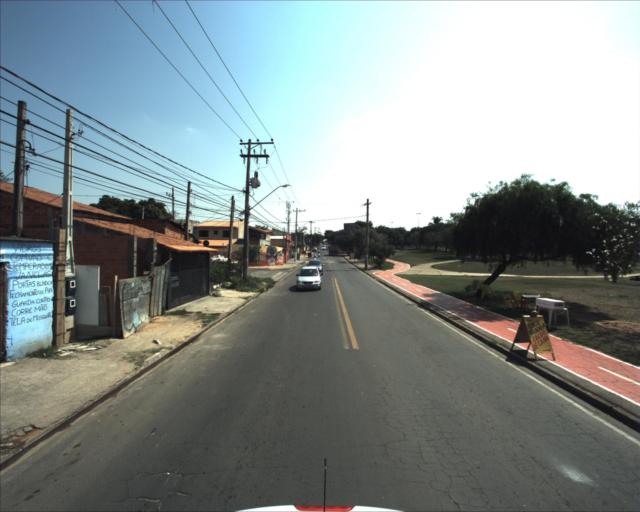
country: BR
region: Sao Paulo
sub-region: Sorocaba
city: Sorocaba
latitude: -23.4317
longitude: -47.4537
